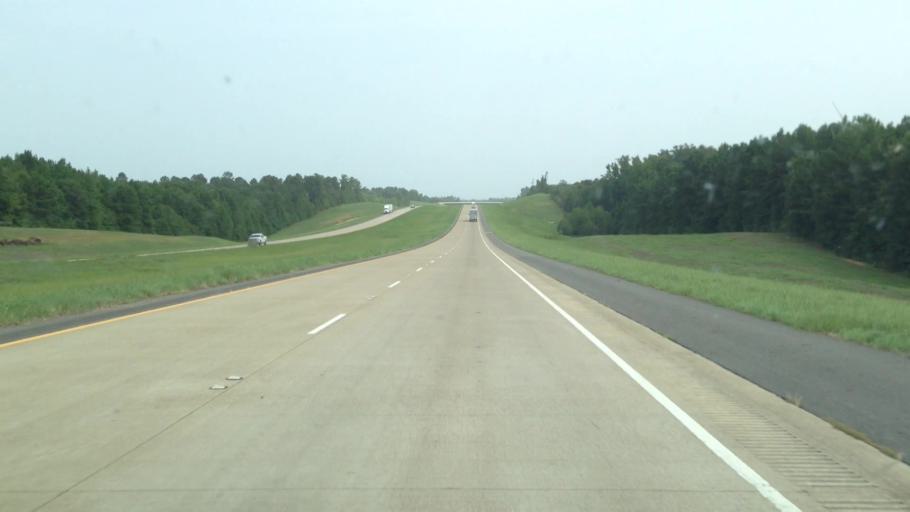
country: US
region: Louisiana
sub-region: Caddo Parish
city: Vivian
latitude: 32.9643
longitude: -93.9044
